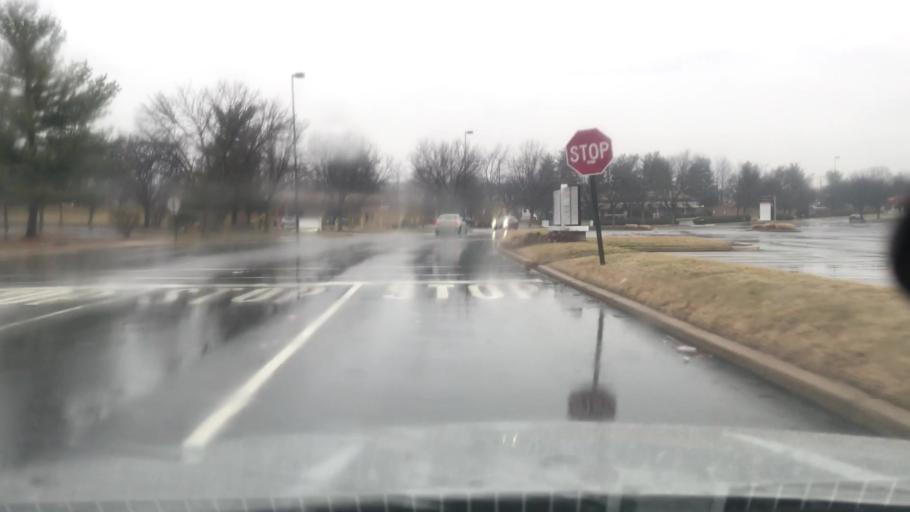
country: US
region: Pennsylvania
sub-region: Bucks County
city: Eddington
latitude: 40.0906
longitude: -74.9635
